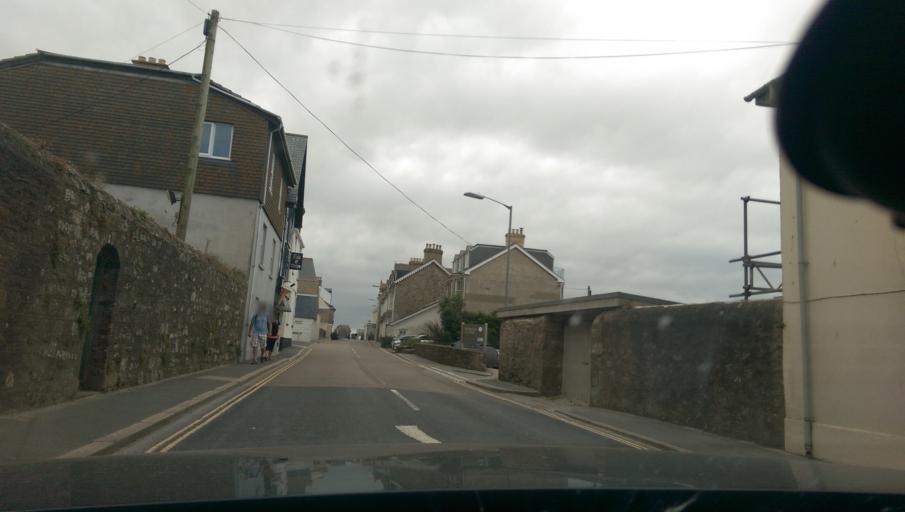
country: GB
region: England
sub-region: Cornwall
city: Marazion
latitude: 50.1246
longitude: -5.4759
